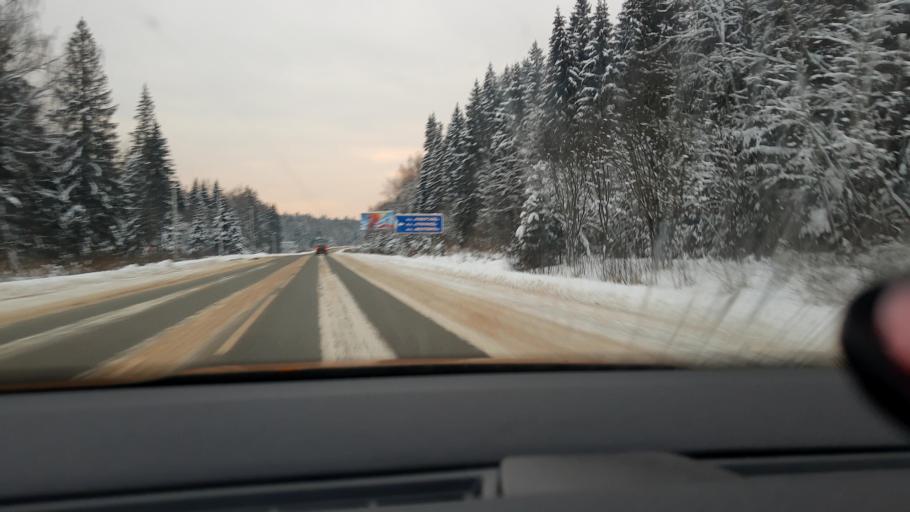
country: RU
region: Moskovskaya
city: Yershovo
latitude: 55.8021
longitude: 36.9459
